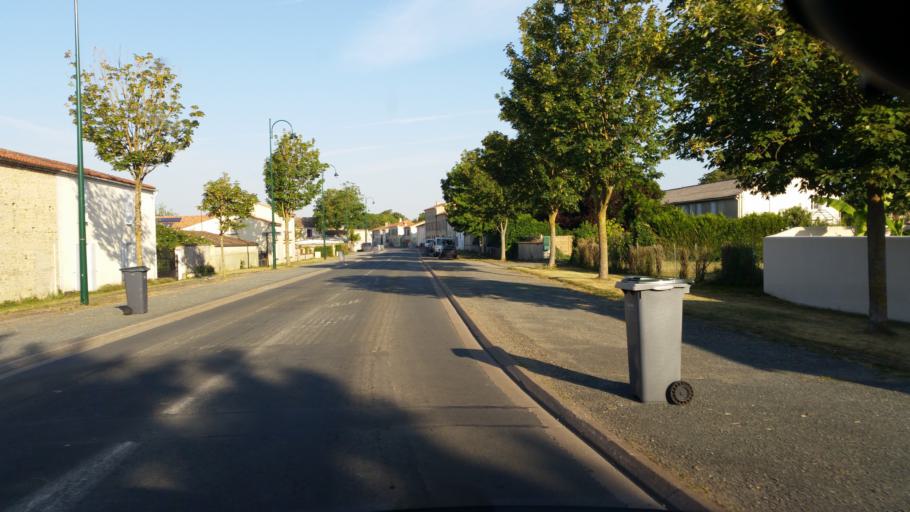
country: FR
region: Poitou-Charentes
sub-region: Departement de la Charente-Maritime
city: Saint-Jean-de-Liversay
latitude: 46.2271
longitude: -0.8577
